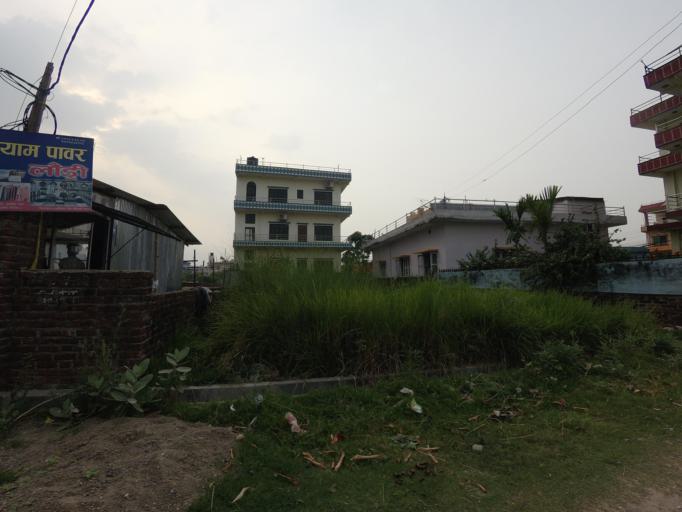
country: NP
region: Western Region
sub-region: Lumbini Zone
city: Bhairahawa
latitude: 27.5203
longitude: 83.4434
